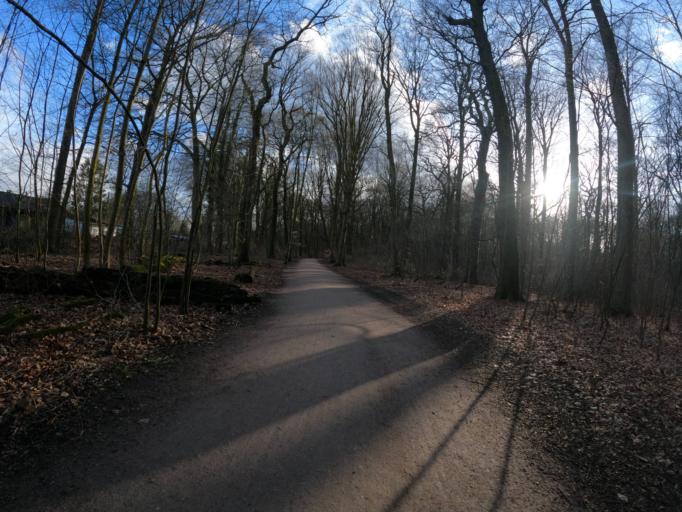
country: DE
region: Hamburg
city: Stellingen
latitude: 53.6117
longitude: 9.9402
